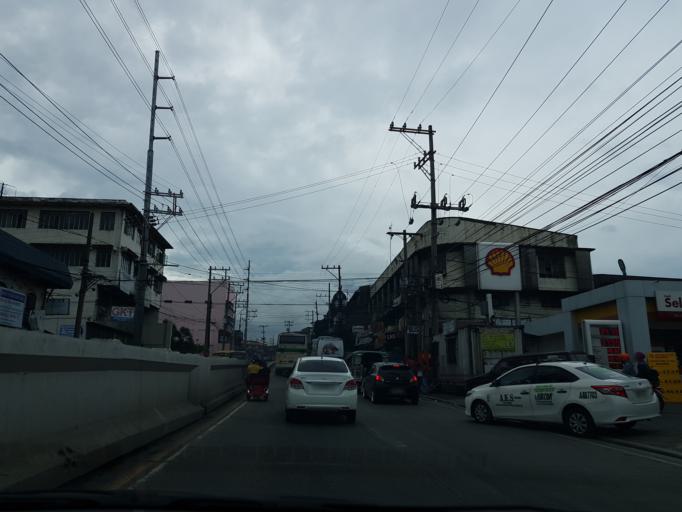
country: PH
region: Metro Manila
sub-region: Caloocan City
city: Niugan
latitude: 14.6699
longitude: 120.9820
